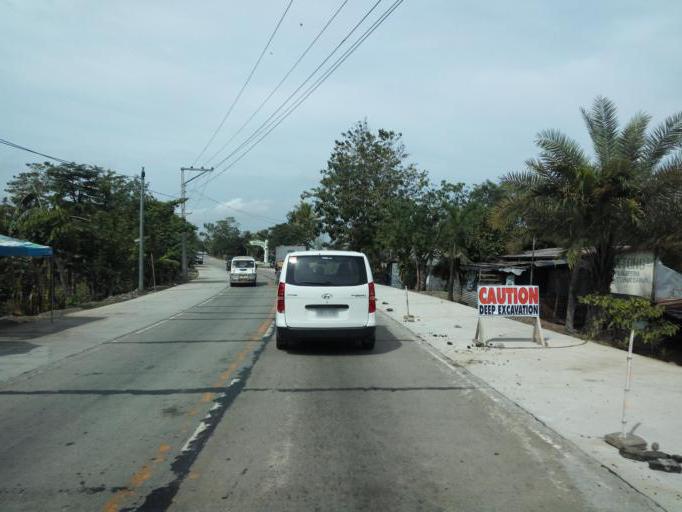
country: PH
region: Cagayan Valley
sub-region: Province of Isabela
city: Gamu
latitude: 17.0471
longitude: 121.8572
